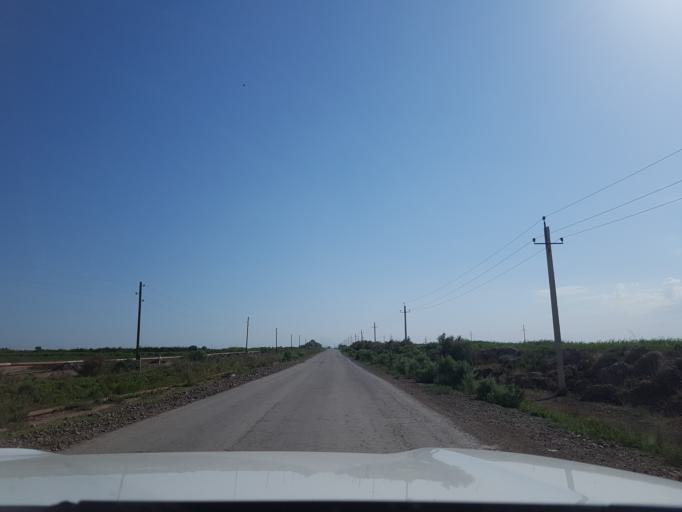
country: TM
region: Dasoguz
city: Koeneuergench
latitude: 42.0930
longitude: 58.8917
